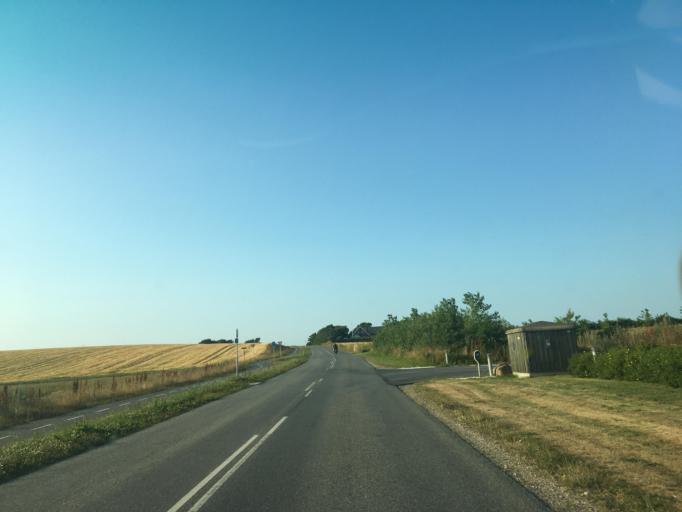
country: DK
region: North Denmark
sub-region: Thisted Kommune
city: Hurup
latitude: 56.7723
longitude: 8.4228
